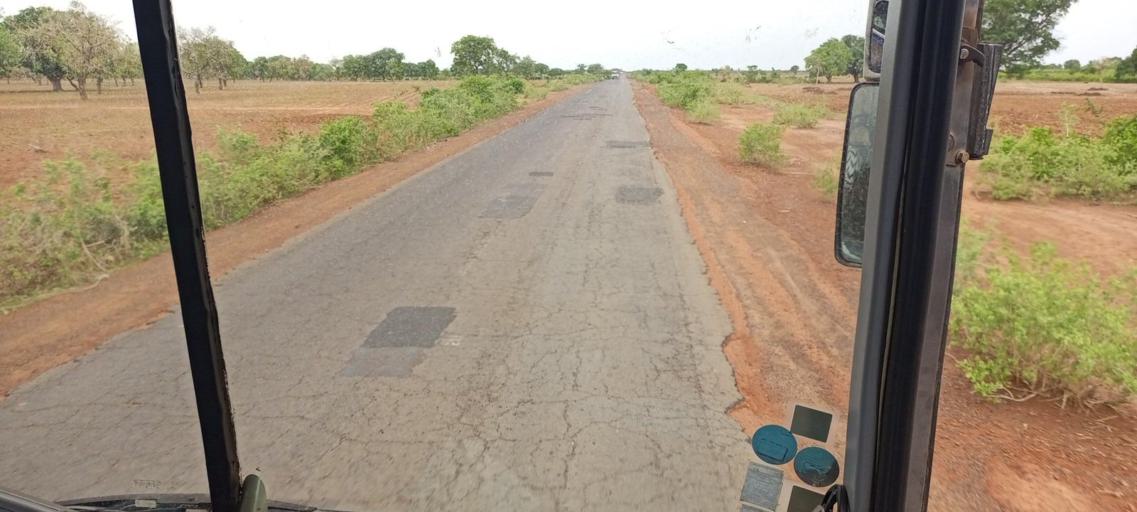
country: ML
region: Segou
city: Bla
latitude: 12.7146
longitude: -5.7247
